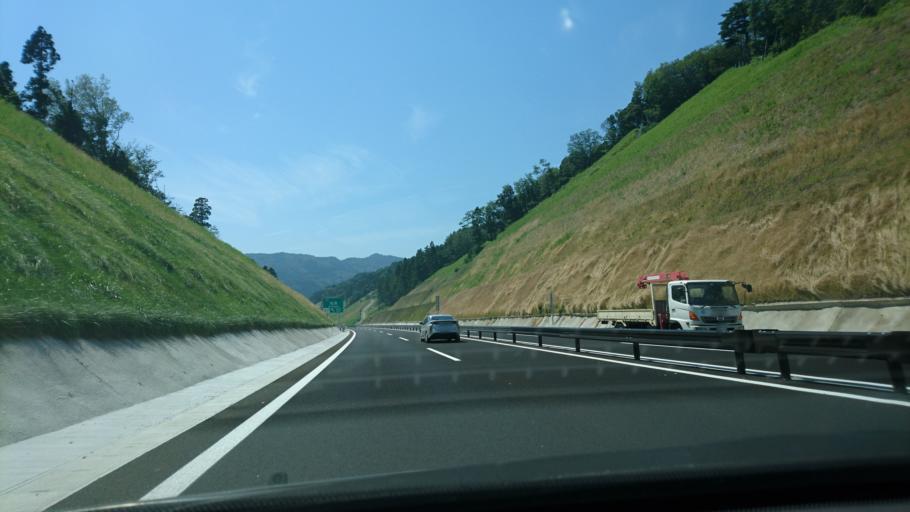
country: JP
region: Iwate
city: Kamaishi
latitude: 39.1540
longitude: 141.8349
